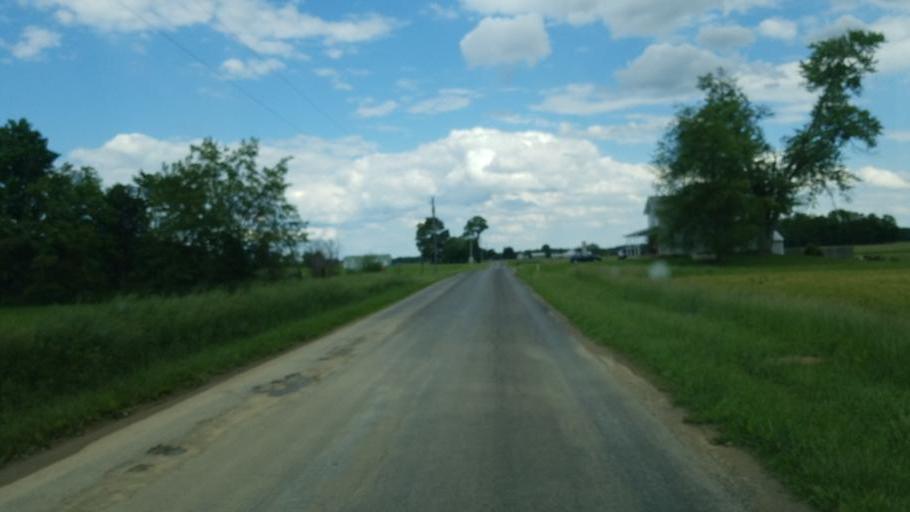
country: US
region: Ohio
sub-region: Huron County
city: Plymouth
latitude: 40.9451
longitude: -82.6359
